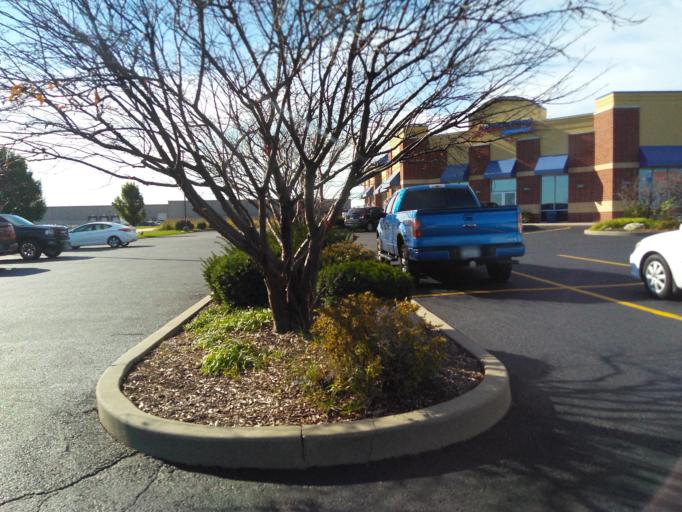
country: US
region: Illinois
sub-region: Madison County
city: Troy
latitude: 38.7162
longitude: -89.9105
